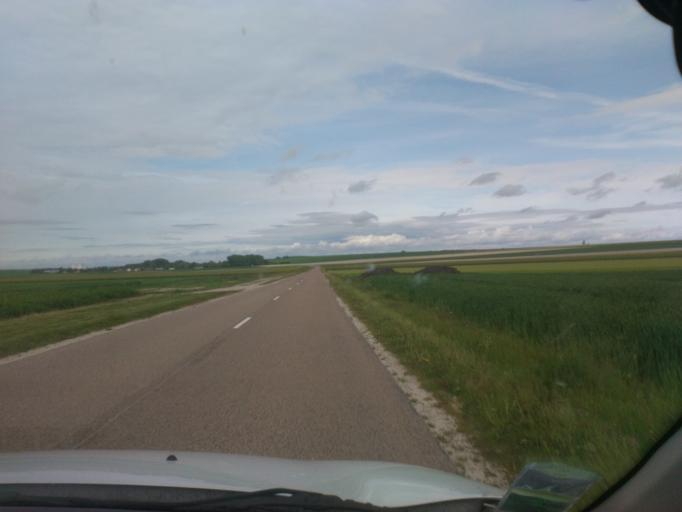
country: FR
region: Champagne-Ardenne
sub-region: Departement de l'Aube
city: Marigny-le-Chatel
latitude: 48.3616
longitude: 3.7327
